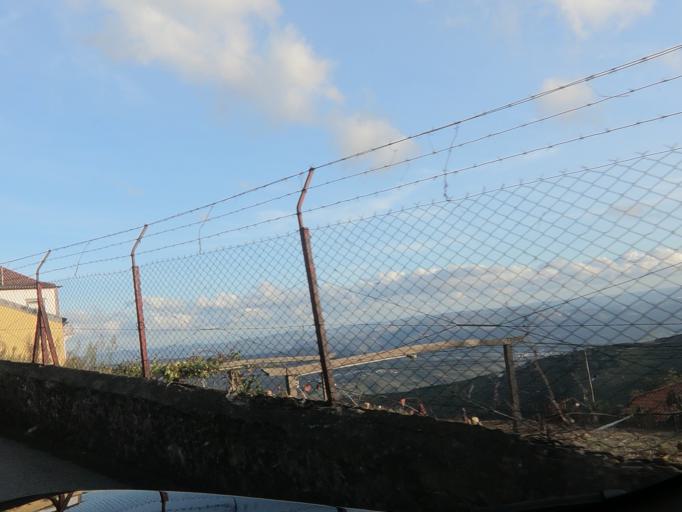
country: PT
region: Vila Real
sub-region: Santa Marta de Penaguiao
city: Santa Marta de Penaguiao
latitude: 41.2292
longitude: -7.8113
